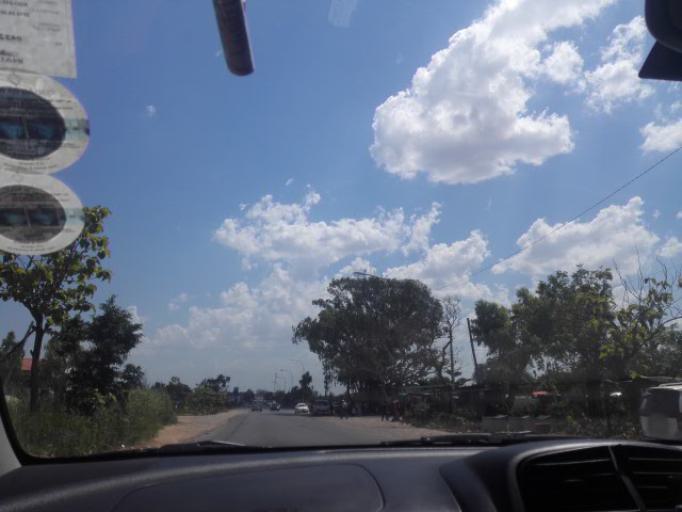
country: MZ
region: Maputo
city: Matola
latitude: -25.9694
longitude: 32.4423
